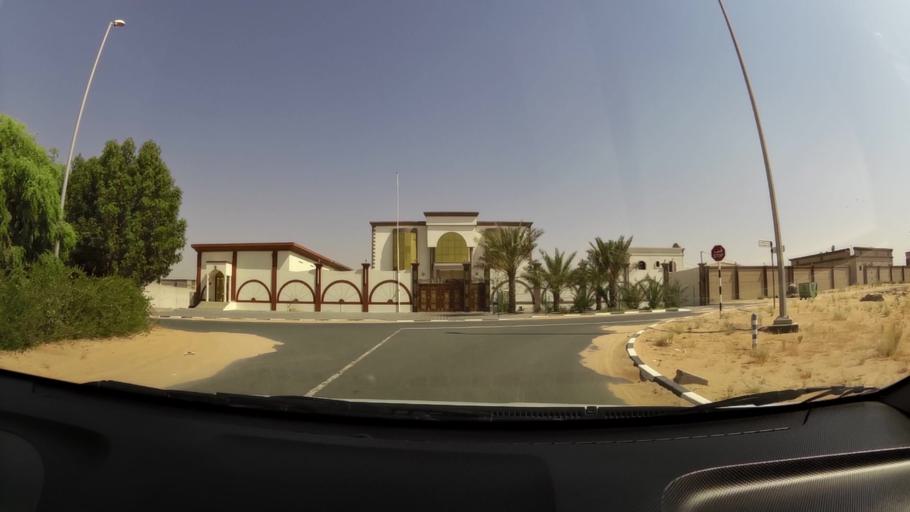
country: AE
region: Umm al Qaywayn
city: Umm al Qaywayn
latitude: 25.4865
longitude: 55.6117
